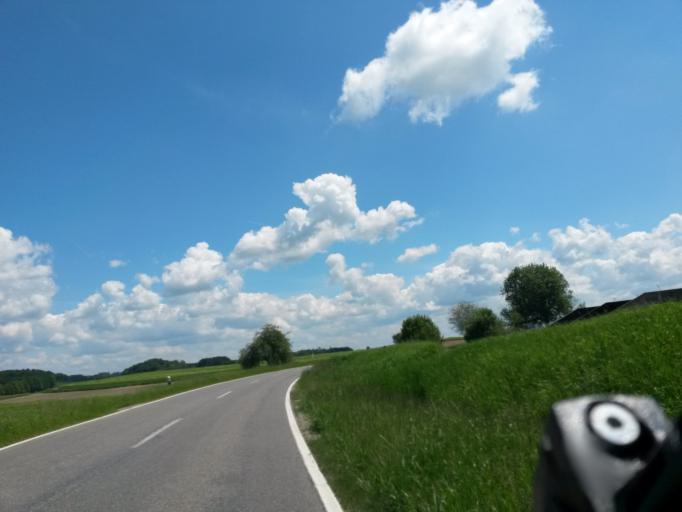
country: DE
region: Baden-Wuerttemberg
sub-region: Tuebingen Region
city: Bad Schussenried
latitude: 48.0052
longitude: 9.6878
